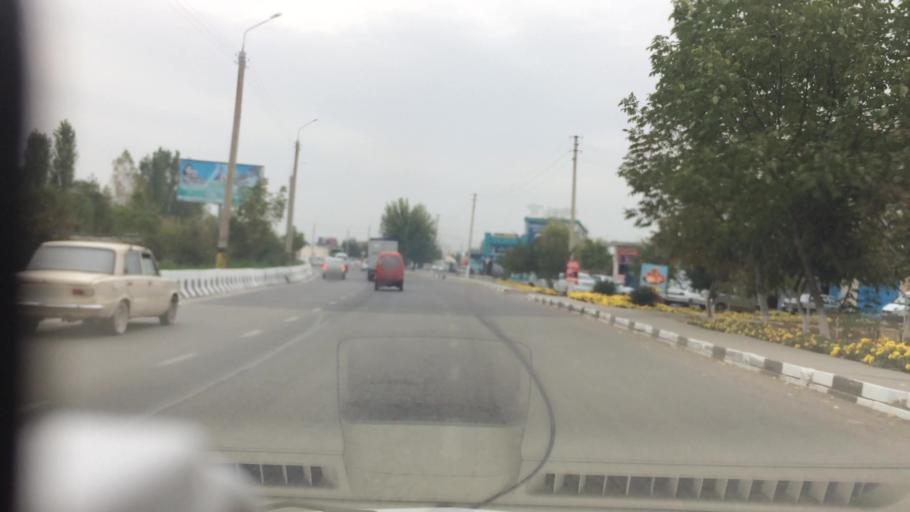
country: UZ
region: Toshkent
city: Salor
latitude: 41.3073
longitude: 69.3427
